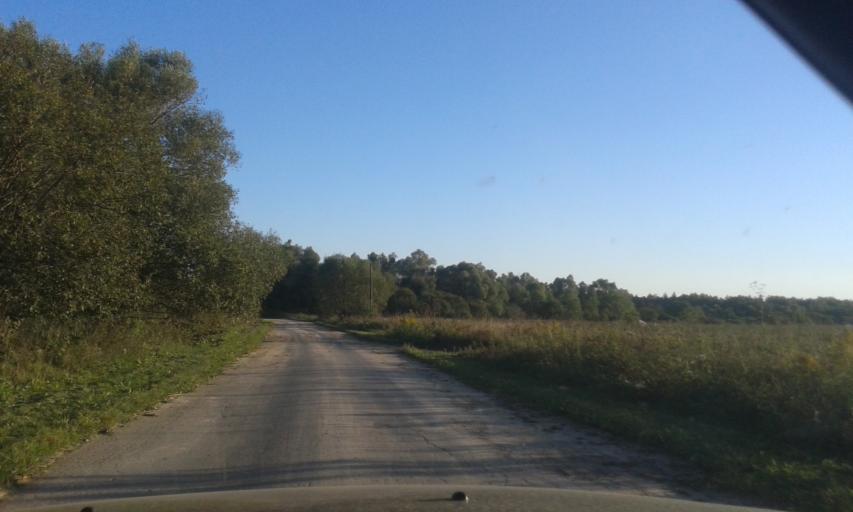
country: RU
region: Tula
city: Krapivna
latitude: 54.1224
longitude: 37.1534
